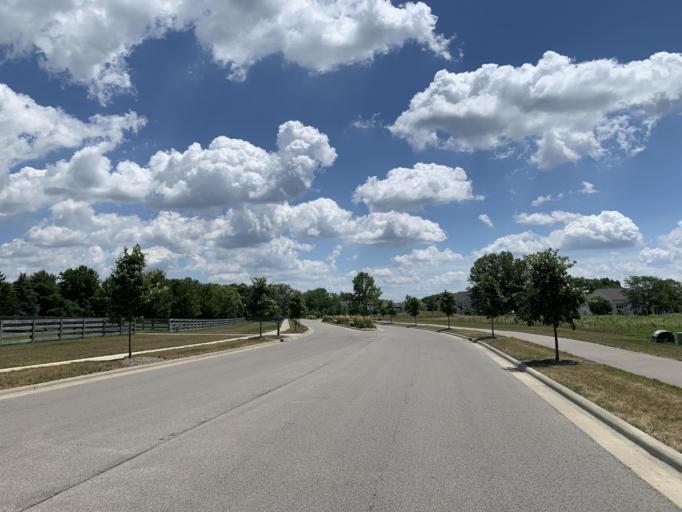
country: US
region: Ohio
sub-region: Union County
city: New California
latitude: 40.1392
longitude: -83.1759
